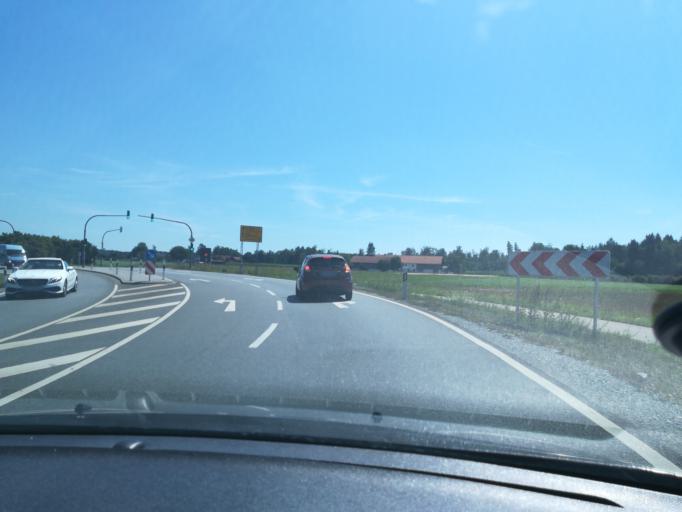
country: DE
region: Bavaria
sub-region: Upper Bavaria
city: Hohenlinden
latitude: 48.1522
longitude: 11.9878
